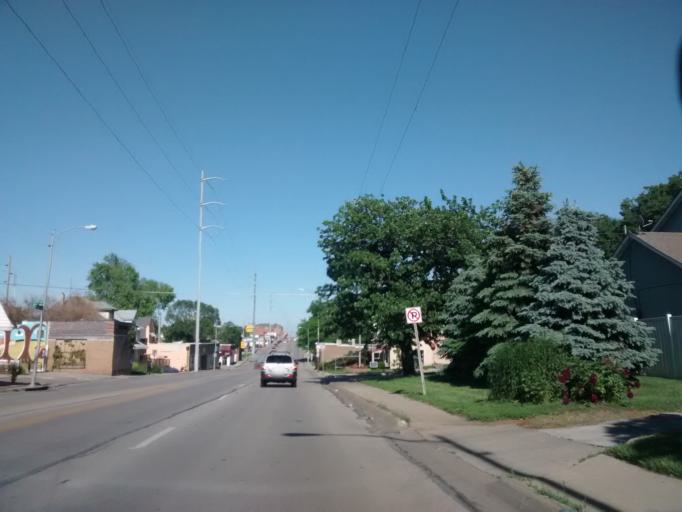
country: US
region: Nebraska
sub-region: Douglas County
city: Omaha
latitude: 41.2523
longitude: -95.9656
